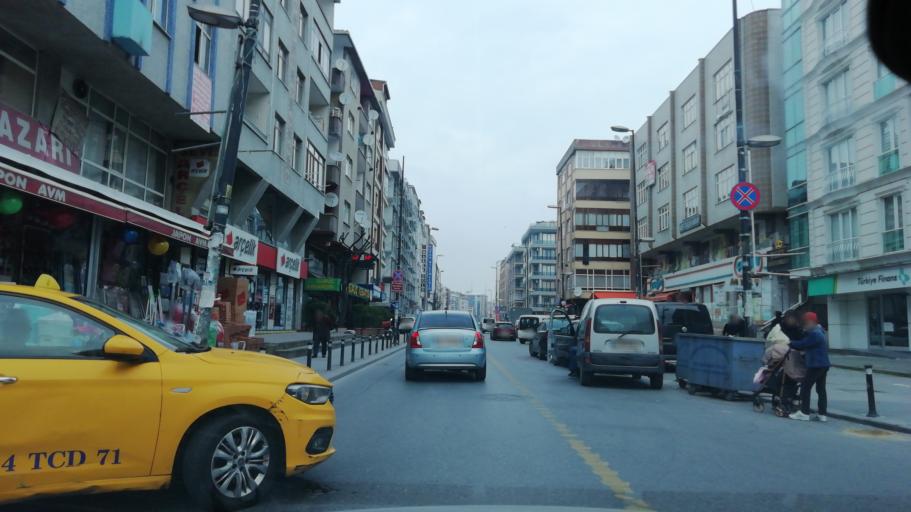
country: TR
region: Istanbul
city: Bahcelievler
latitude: 41.0088
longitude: 28.8414
